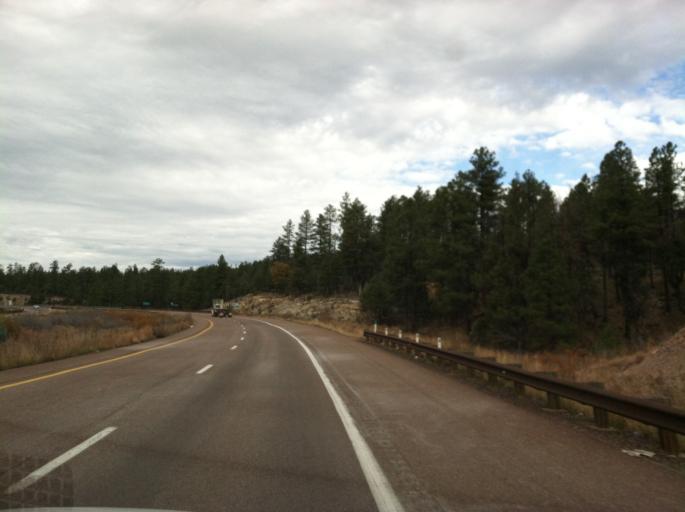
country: US
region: Arizona
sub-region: Gila County
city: Star Valley
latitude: 34.3130
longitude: -111.0276
